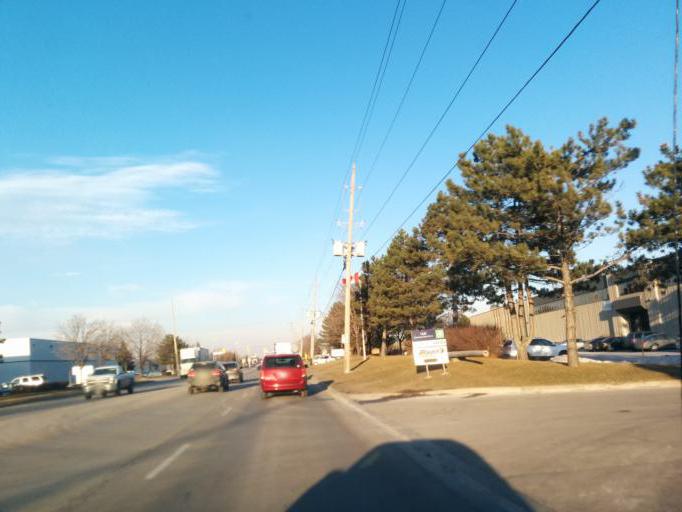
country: CA
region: Ontario
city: Mississauga
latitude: 43.6605
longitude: -79.6614
